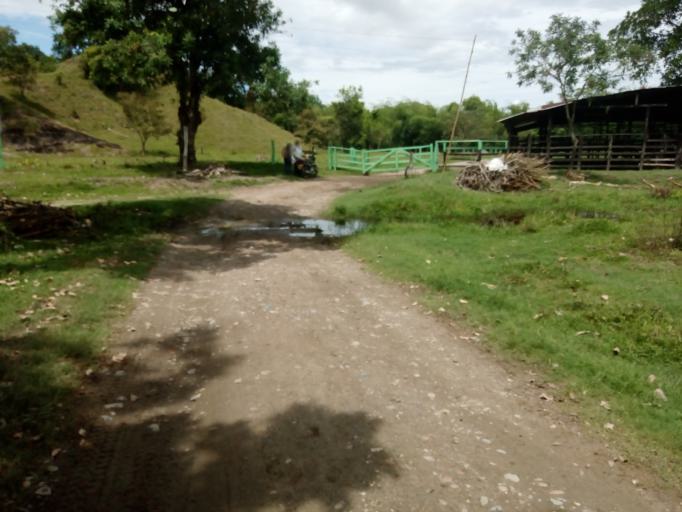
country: CO
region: Boyaca
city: Puerto Boyaca
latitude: 6.0139
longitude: -74.3946
